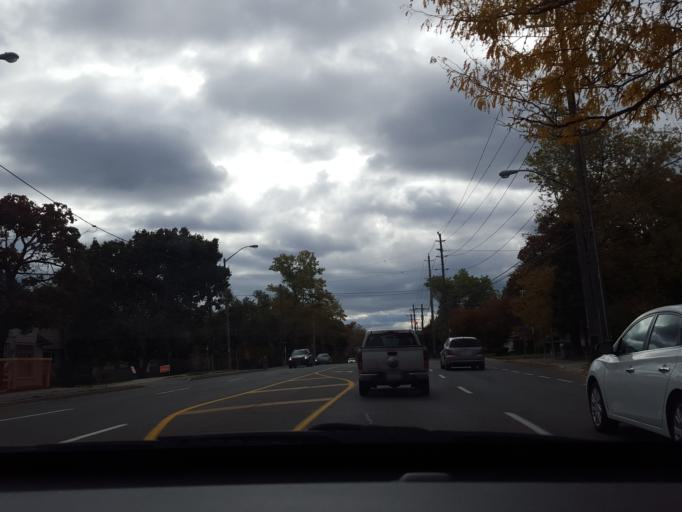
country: CA
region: Ontario
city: Scarborough
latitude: 43.7997
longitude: -79.2955
